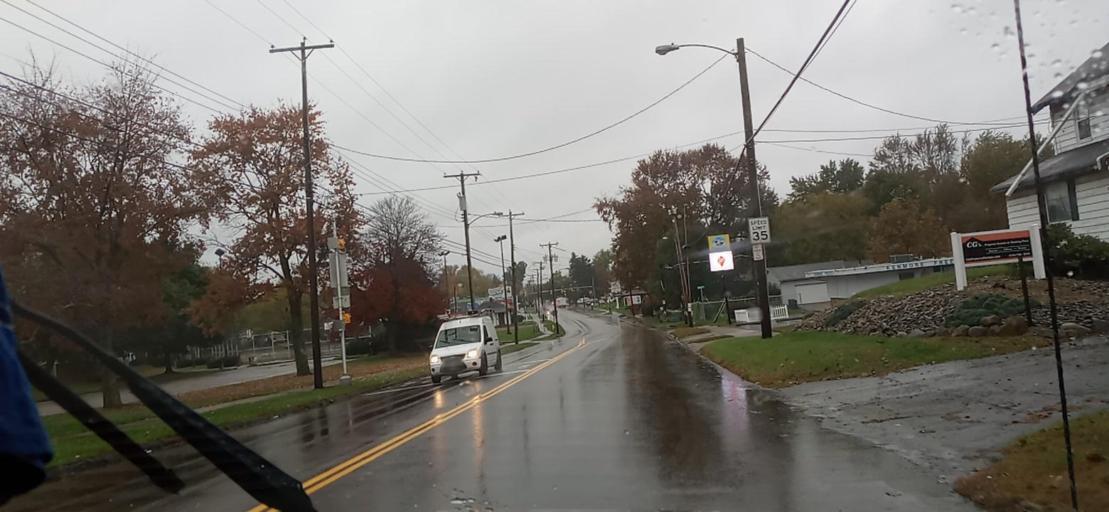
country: US
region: Ohio
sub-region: Summit County
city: Barberton
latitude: 41.0486
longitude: -81.5688
